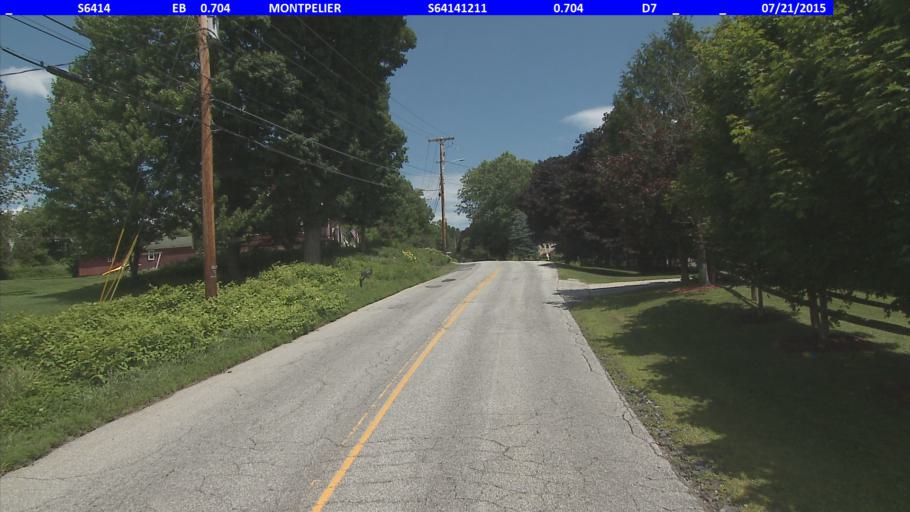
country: US
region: Vermont
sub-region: Washington County
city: Montpelier
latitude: 44.2440
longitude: -72.5314
